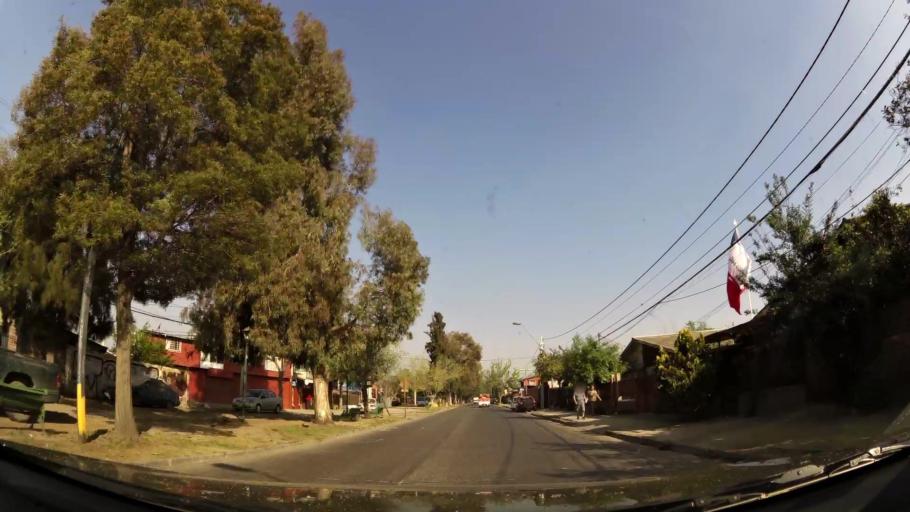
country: CL
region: Santiago Metropolitan
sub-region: Provincia de Santiago
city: Lo Prado
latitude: -33.3747
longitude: -70.6908
